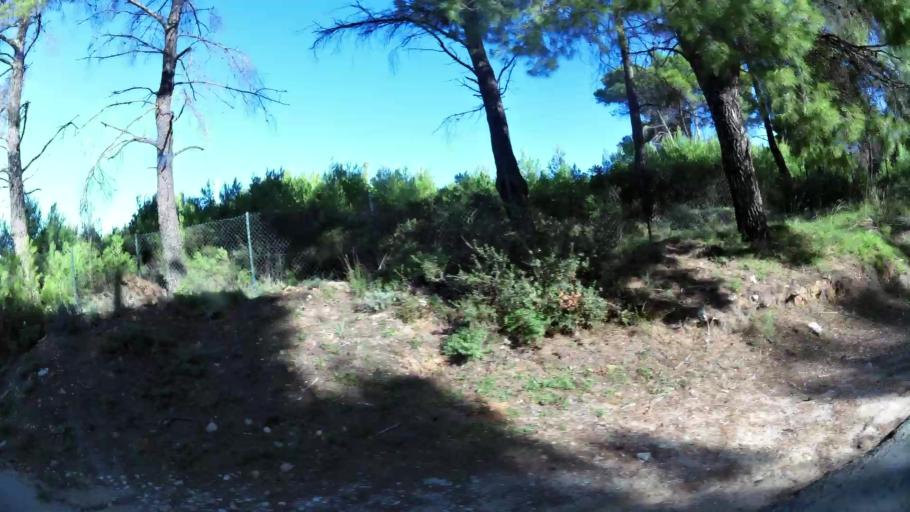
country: GR
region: Attica
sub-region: Nomarchia Anatolikis Attikis
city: Drosia
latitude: 38.1261
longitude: 23.8704
